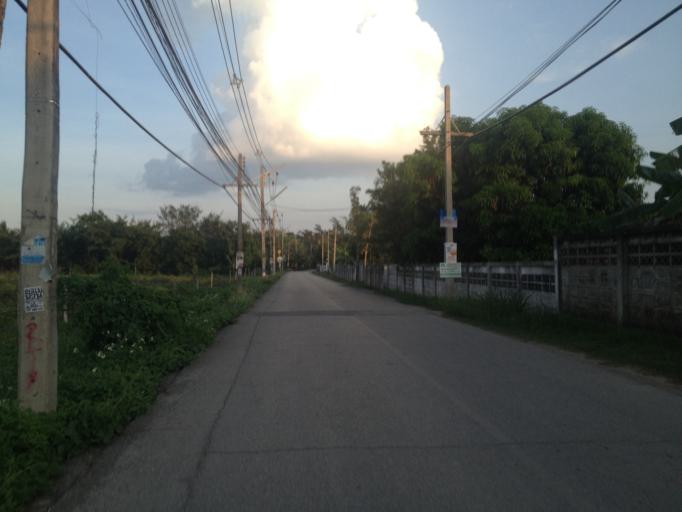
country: TH
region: Chiang Mai
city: Chiang Mai
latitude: 18.7631
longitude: 98.9501
